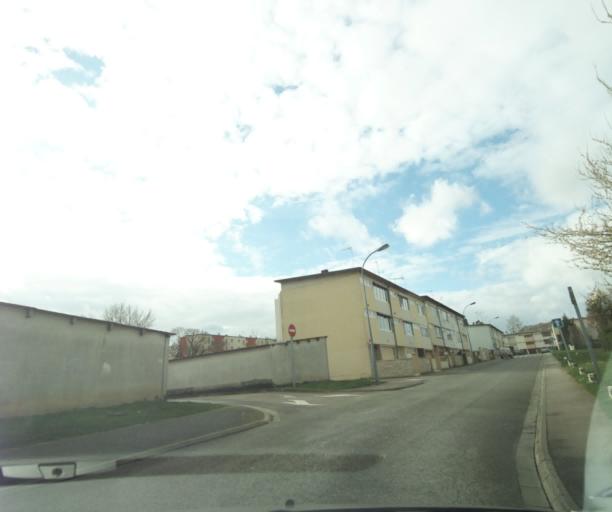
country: FR
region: Picardie
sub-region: Departement de l'Oise
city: Noyon
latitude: 49.5803
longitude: 2.9901
